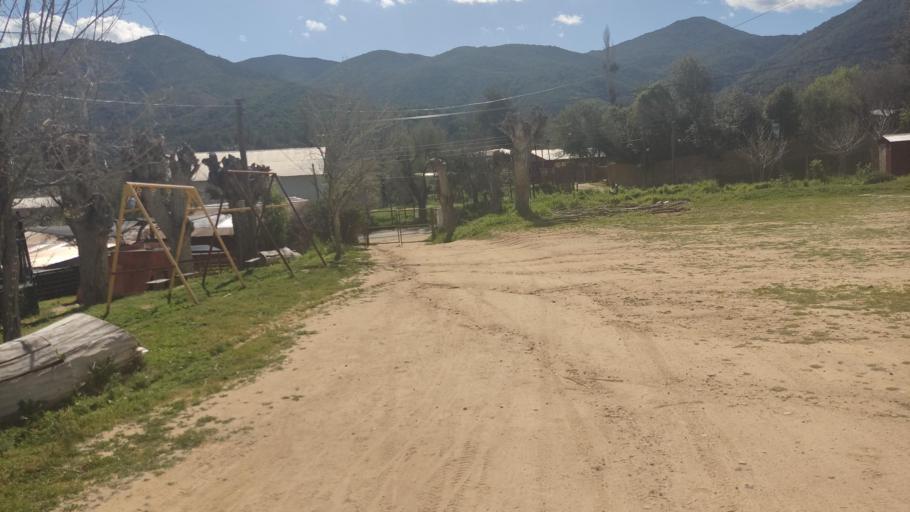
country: CL
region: Valparaiso
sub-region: Provincia de Marga Marga
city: Limache
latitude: -33.1730
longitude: -71.1651
